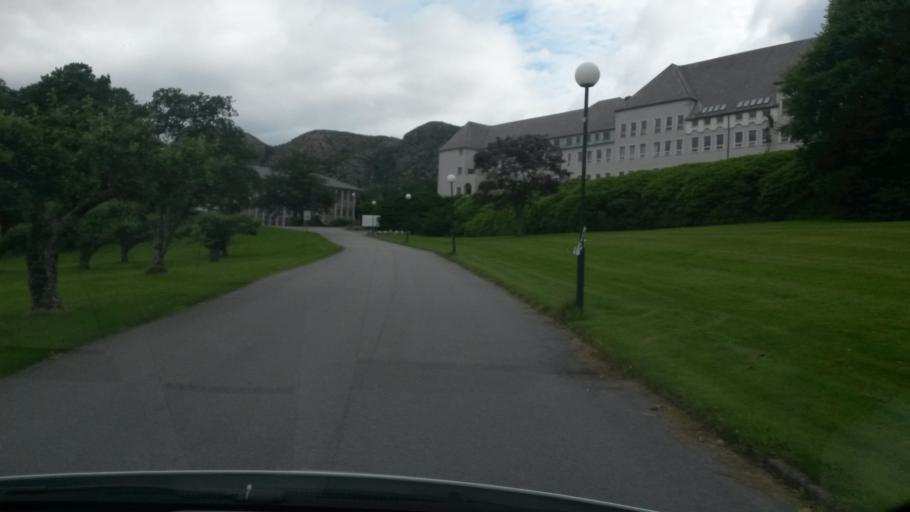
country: NO
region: Rogaland
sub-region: Sandnes
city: Sandnes
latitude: 58.8982
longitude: 5.7778
